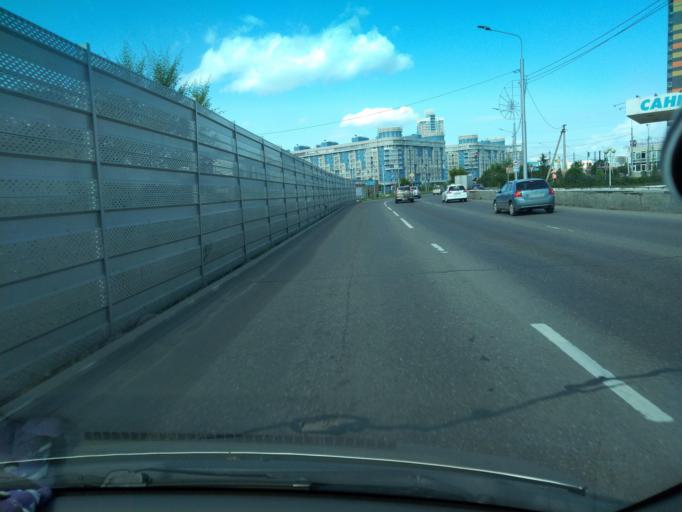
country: RU
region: Krasnoyarskiy
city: Krasnoyarsk
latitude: 56.0469
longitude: 92.9186
